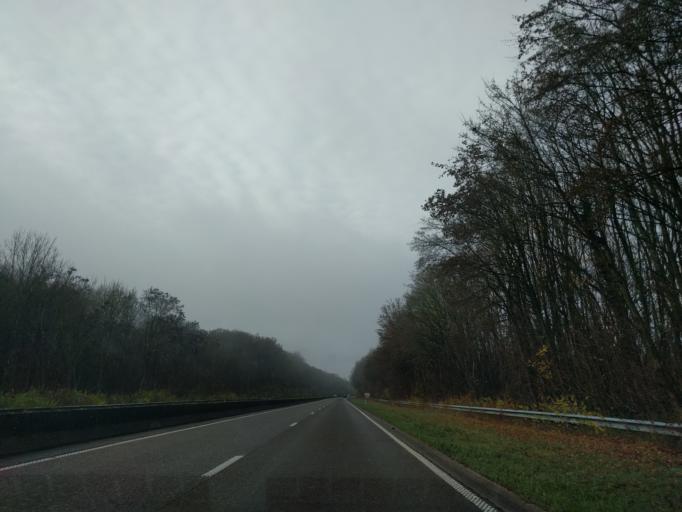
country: BE
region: Wallonia
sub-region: Province de Namur
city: Onhaye
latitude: 50.2428
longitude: 4.8775
